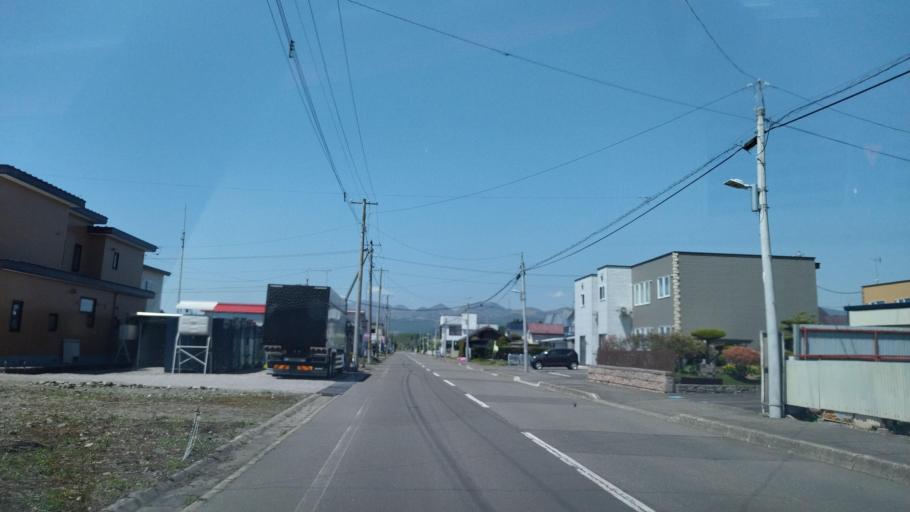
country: JP
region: Hokkaido
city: Otofuke
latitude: 43.2307
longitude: 143.2873
